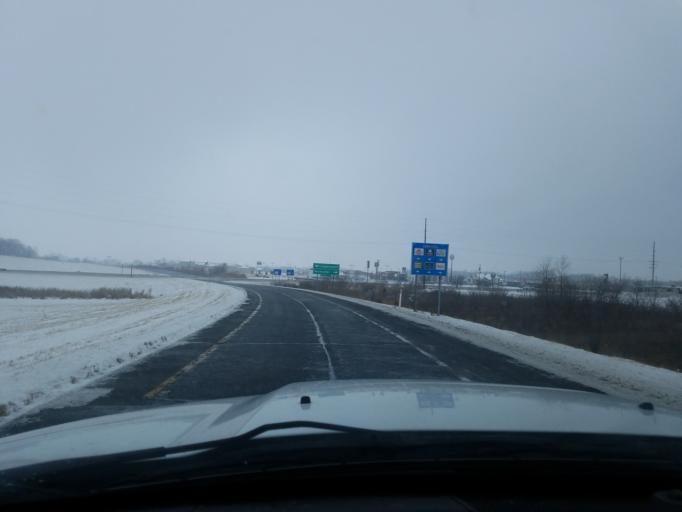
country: US
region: Indiana
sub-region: Fulton County
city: Rochester
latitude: 41.0465
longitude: -86.2172
